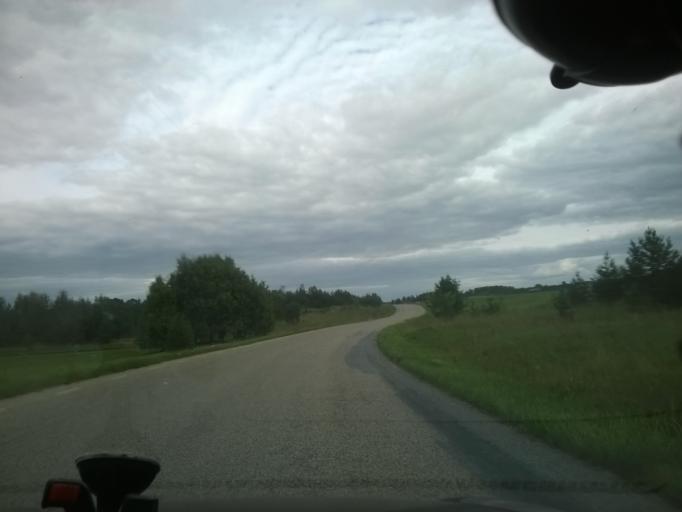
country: EE
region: Vorumaa
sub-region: Voru linn
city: Voru
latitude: 57.7435
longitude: 26.9559
